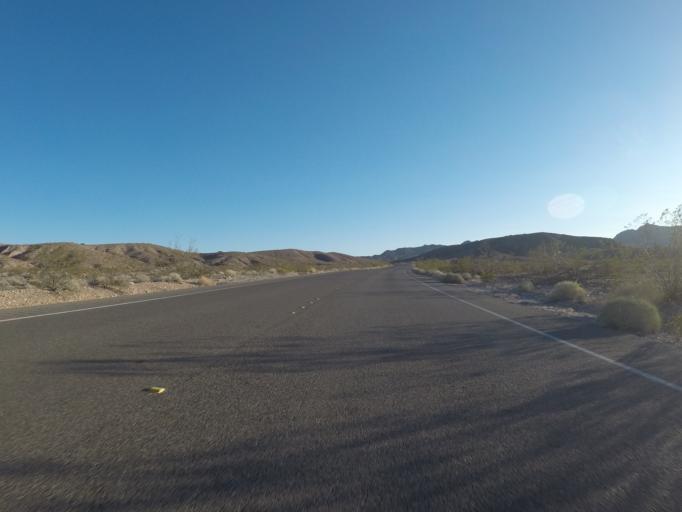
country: US
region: Nevada
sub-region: Clark County
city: Moapa Valley
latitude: 36.2794
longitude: -114.4881
